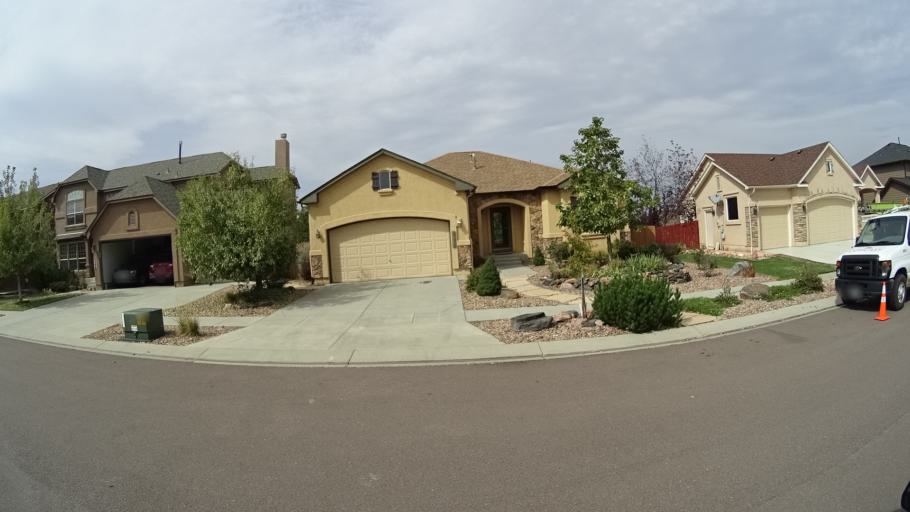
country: US
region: Colorado
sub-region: El Paso County
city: Cimarron Hills
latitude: 38.9221
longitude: -104.6875
